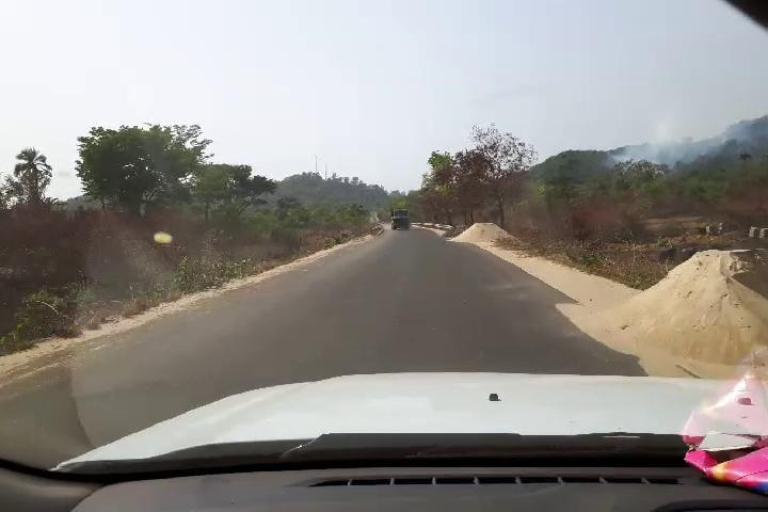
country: SL
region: Western Area
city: Waterloo
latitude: 8.2553
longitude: -13.1573
